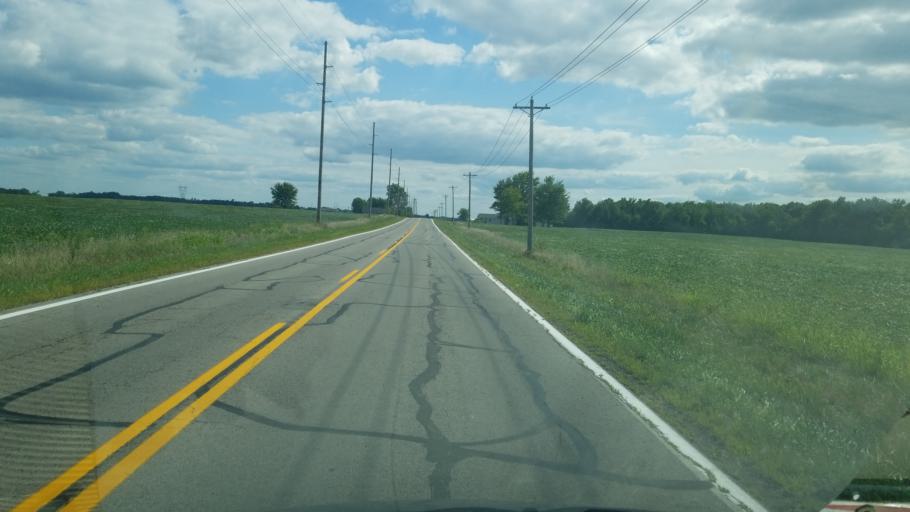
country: US
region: Ohio
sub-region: Logan County
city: Lakeview
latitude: 40.4669
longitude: -83.9176
